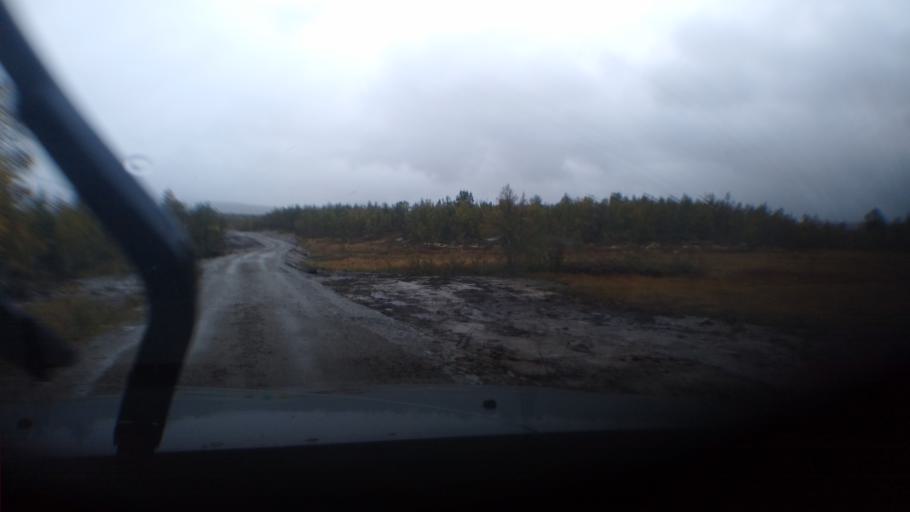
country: NO
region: Oppland
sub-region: Ringebu
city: Ringebu
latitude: 61.6557
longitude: 10.1031
